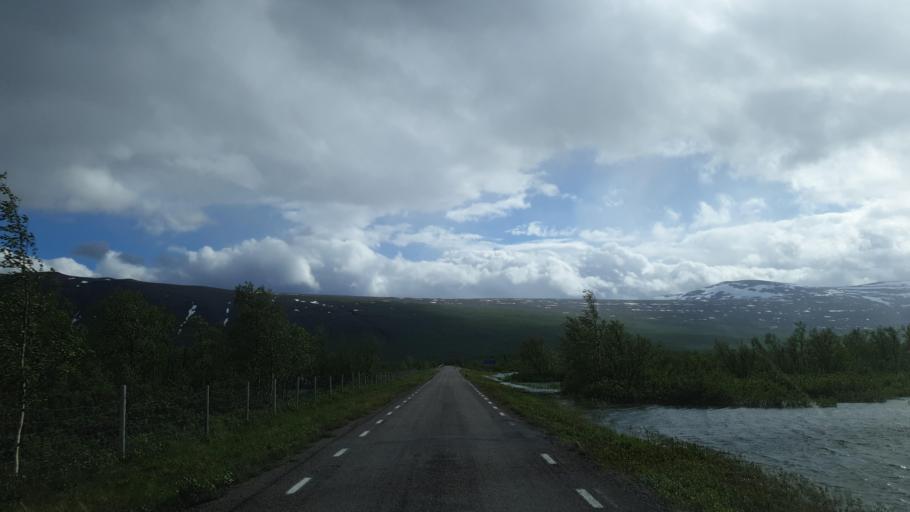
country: SE
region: Norrbotten
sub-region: Kiruna Kommun
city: Kiruna
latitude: 67.8577
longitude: 19.0244
